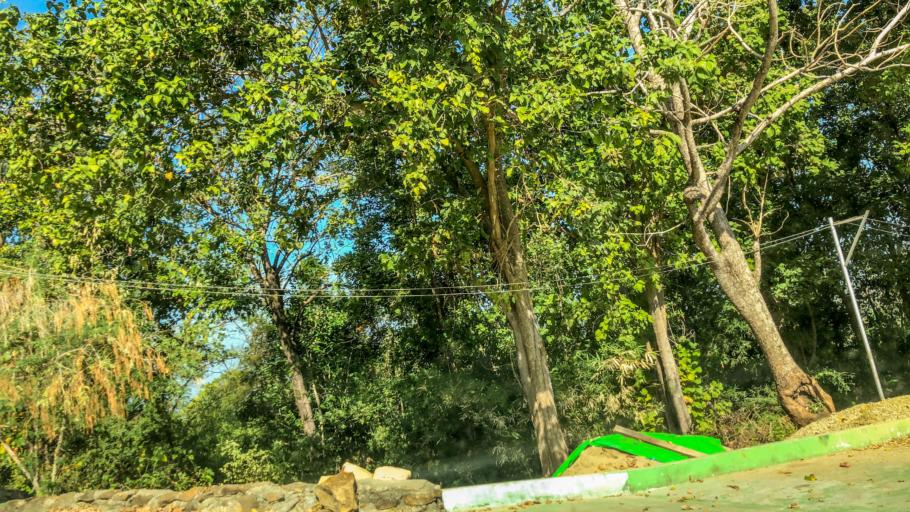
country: MM
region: Magway
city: Magway
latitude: 19.7605
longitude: 94.9365
